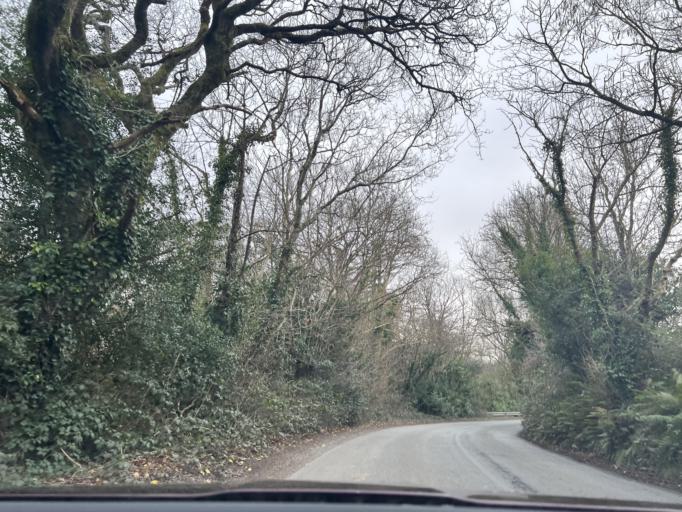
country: IE
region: Leinster
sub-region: Loch Garman
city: Castlebridge
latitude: 52.3809
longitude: -6.5404
